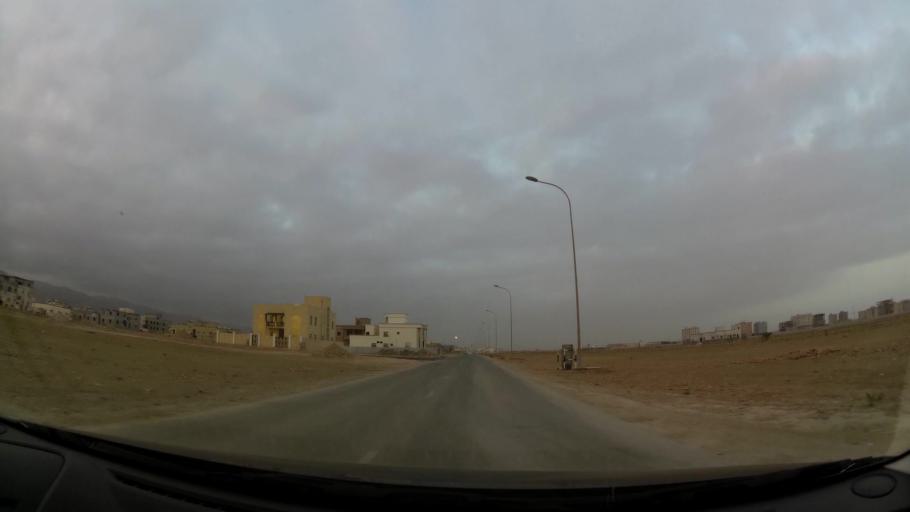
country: OM
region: Zufar
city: Salalah
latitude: 17.0282
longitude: 54.0208
